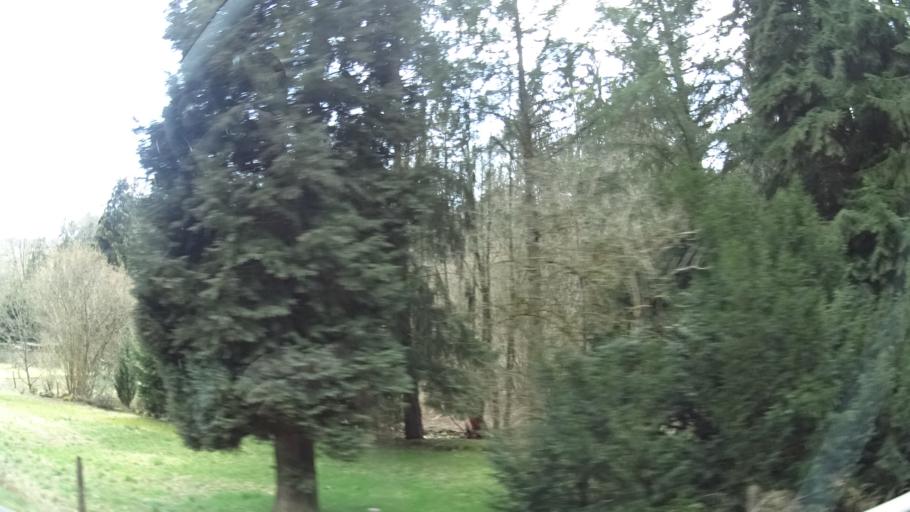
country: DE
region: Rheinland-Pfalz
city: Sensweiler
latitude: 49.7671
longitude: 7.2198
